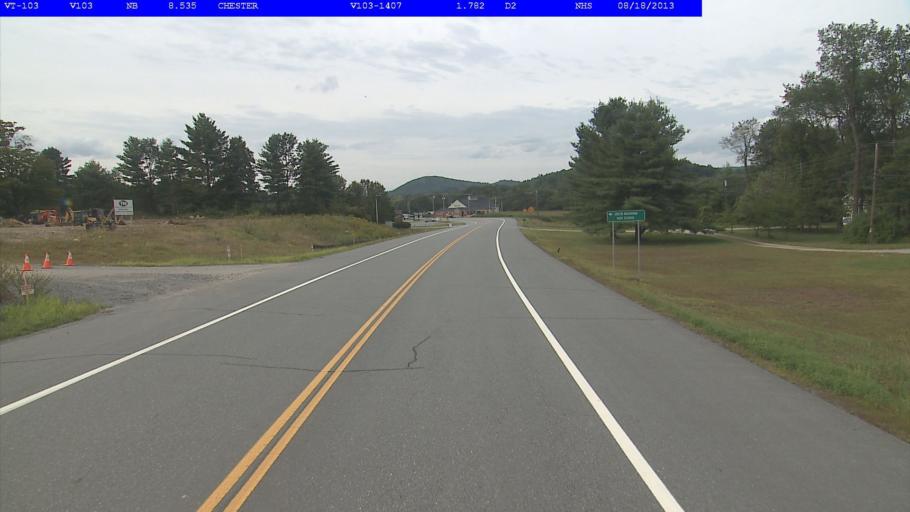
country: US
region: Vermont
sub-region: Windsor County
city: Chester
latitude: 43.2529
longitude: -72.5777
